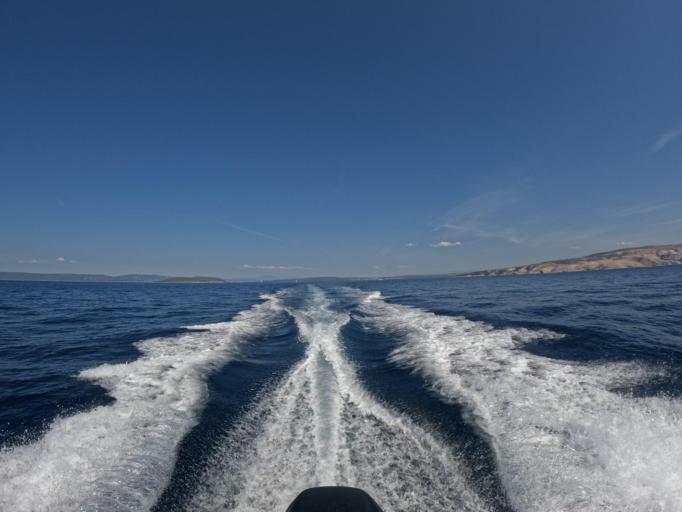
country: HR
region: Primorsko-Goranska
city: Punat
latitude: 44.9188
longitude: 14.6234
